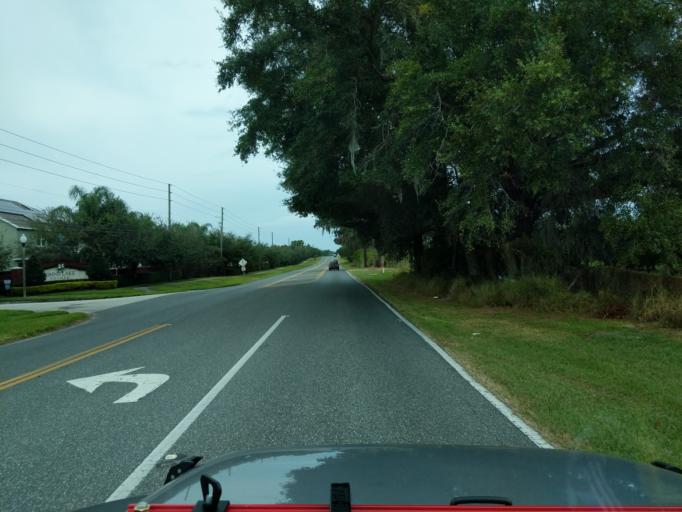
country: US
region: Florida
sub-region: Orange County
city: Oakland
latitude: 28.5327
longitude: -81.6078
